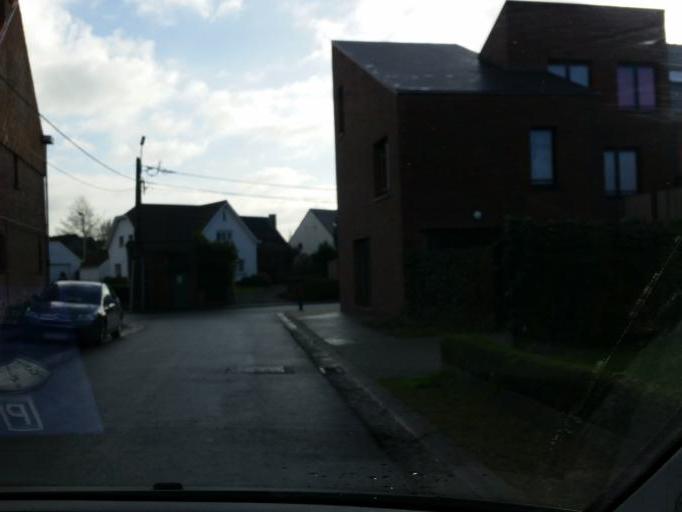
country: BE
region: Flanders
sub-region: Provincie Vlaams-Brabant
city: Zemst
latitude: 50.9673
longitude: 4.4528
